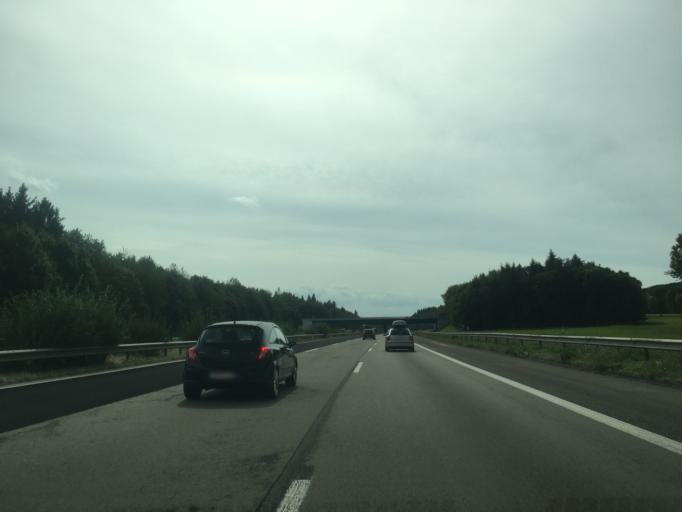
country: DE
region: Rheinland-Pfalz
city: Nortershausen
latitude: 50.2489
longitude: 7.5170
